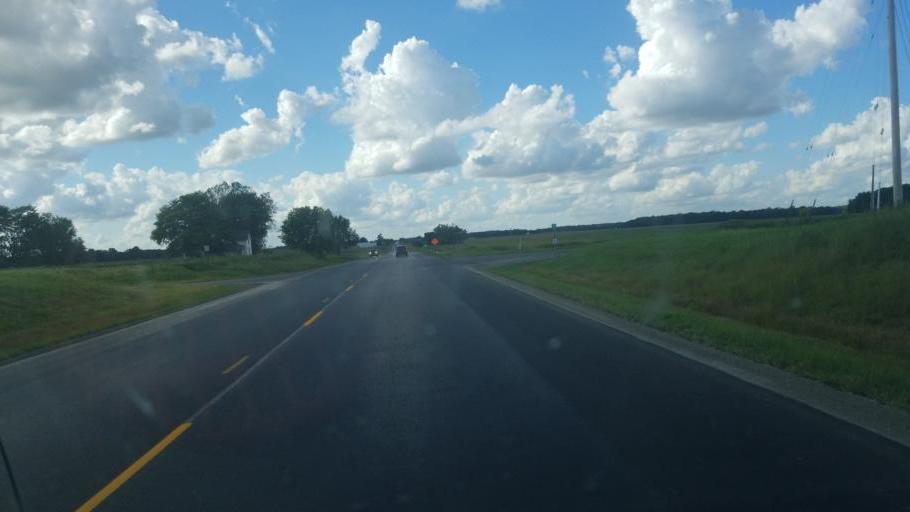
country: US
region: Ohio
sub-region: Hardin County
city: Kenton
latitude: 40.6665
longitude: -83.6543
